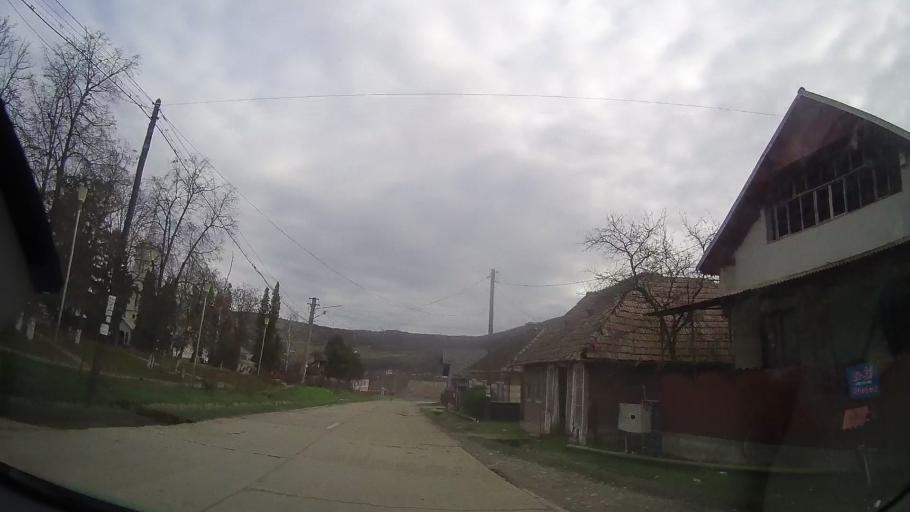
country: RO
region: Bistrita-Nasaud
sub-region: Comuna Sanmihaiu de Campie
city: Sanmihaiu de Campie
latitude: 46.8936
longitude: 24.3318
